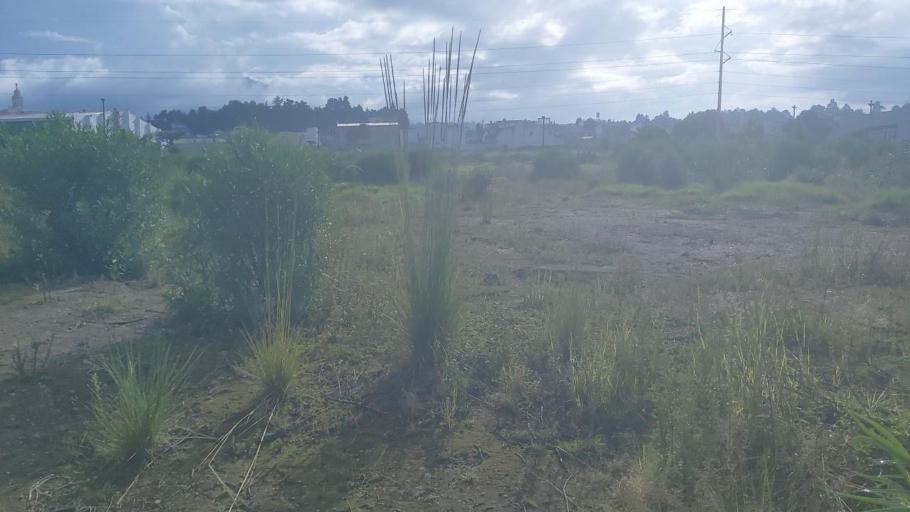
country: GT
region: Quetzaltenango
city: Quetzaltenango
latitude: 14.8496
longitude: -91.5387
